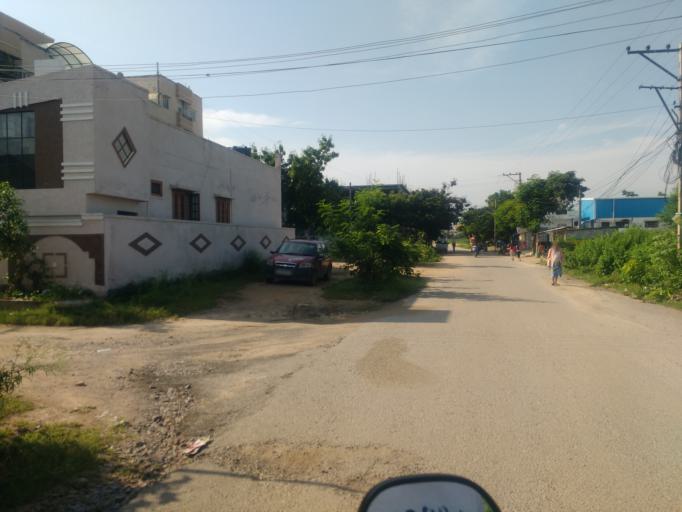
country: IN
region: Telangana
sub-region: Medak
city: Patancheru
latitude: 17.5328
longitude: 78.3018
